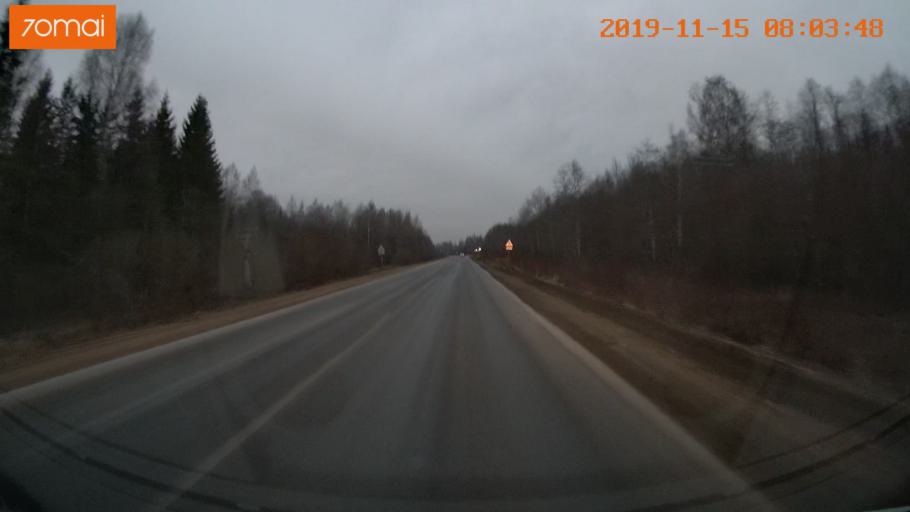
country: RU
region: Vologda
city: Cherepovets
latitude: 59.0017
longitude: 38.0845
